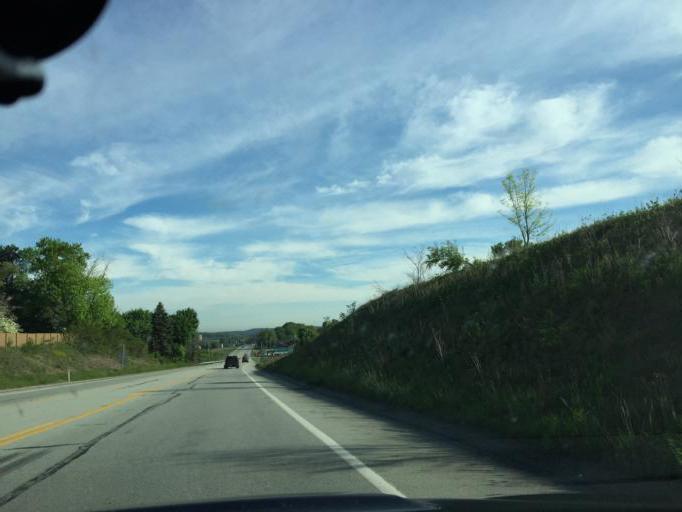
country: US
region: Pennsylvania
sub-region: Westmoreland County
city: Lawson Heights
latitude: 40.2873
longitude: -79.3938
